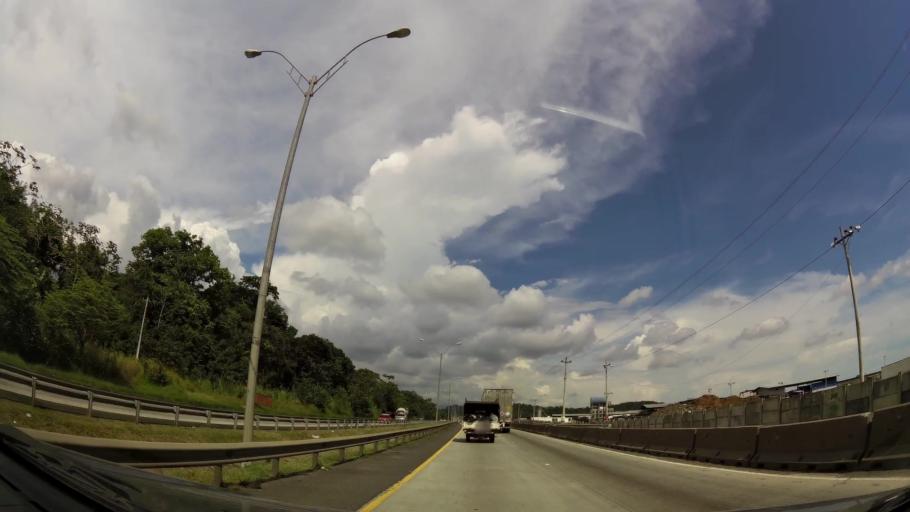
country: PA
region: Panama
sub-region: Distrito de Panama
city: Paraiso
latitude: 9.0301
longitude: -79.5855
